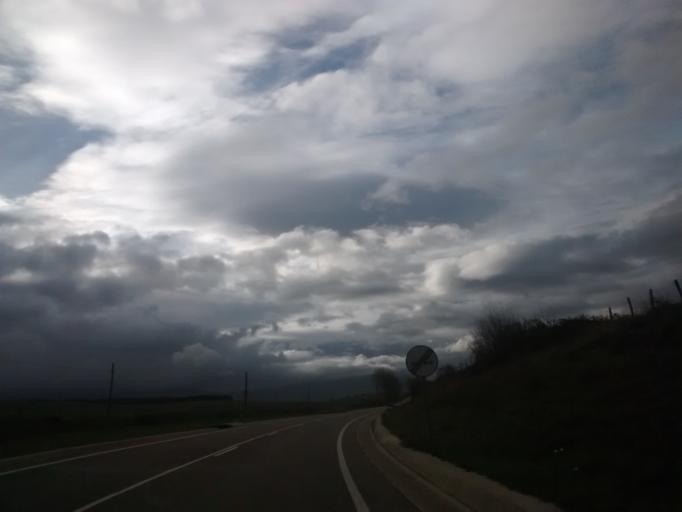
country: ES
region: Cantabria
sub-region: Provincia de Cantabria
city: Santiurde de Reinosa
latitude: 43.0051
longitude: -4.0777
